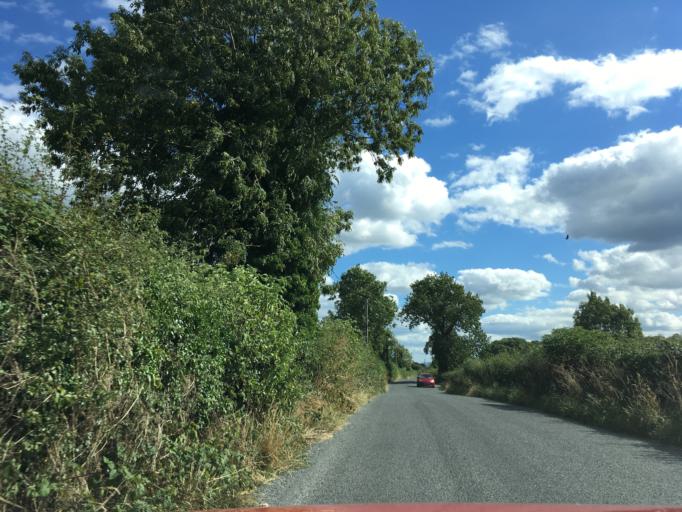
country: IE
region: Munster
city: Cashel
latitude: 52.4707
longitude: -7.9785
